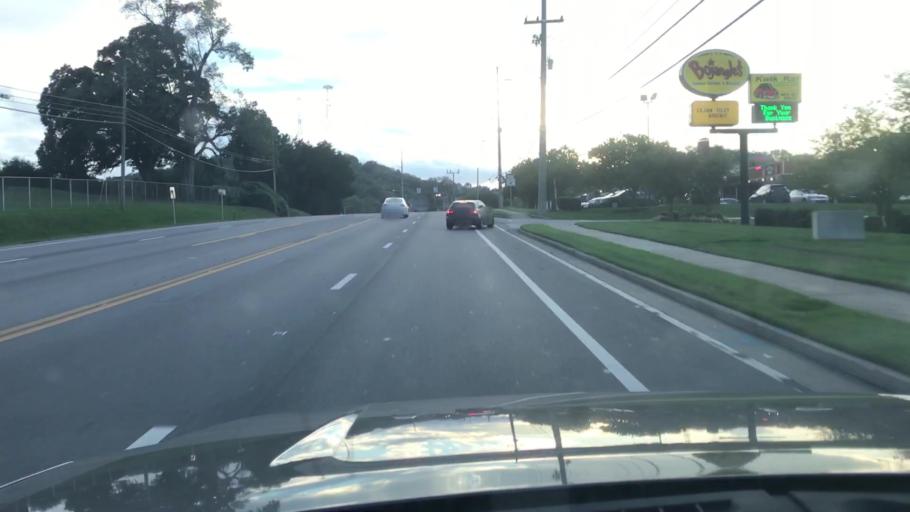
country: US
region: Tennessee
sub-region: Davidson County
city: Belle Meade
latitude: 36.1295
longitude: -86.9038
